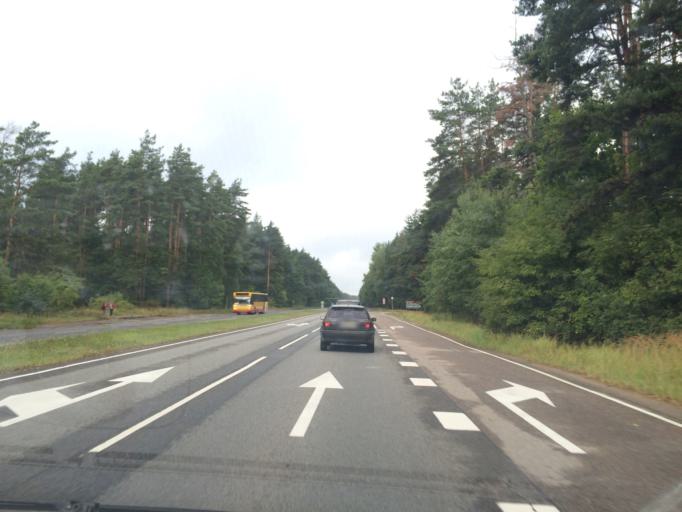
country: LV
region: Salaspils
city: Salaspils
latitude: 56.8602
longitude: 24.3060
